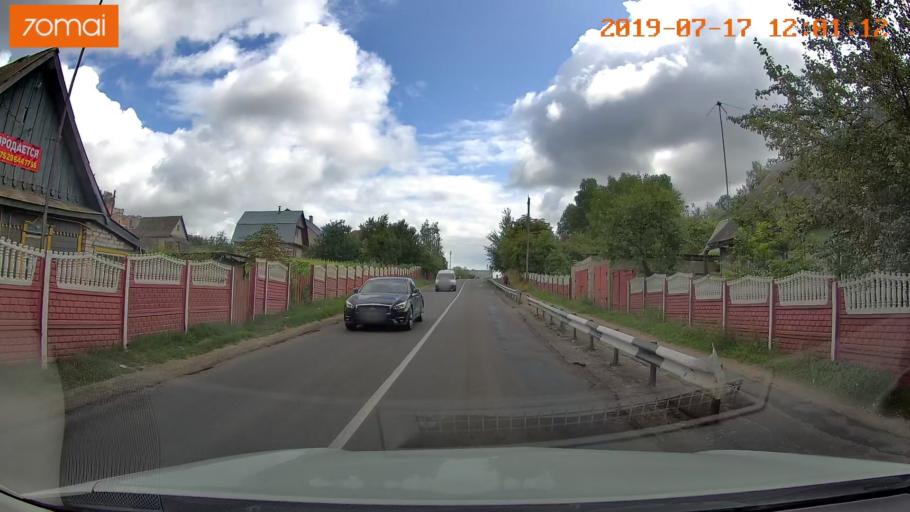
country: BY
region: Minsk
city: Borovlyany
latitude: 54.0047
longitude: 27.6736
